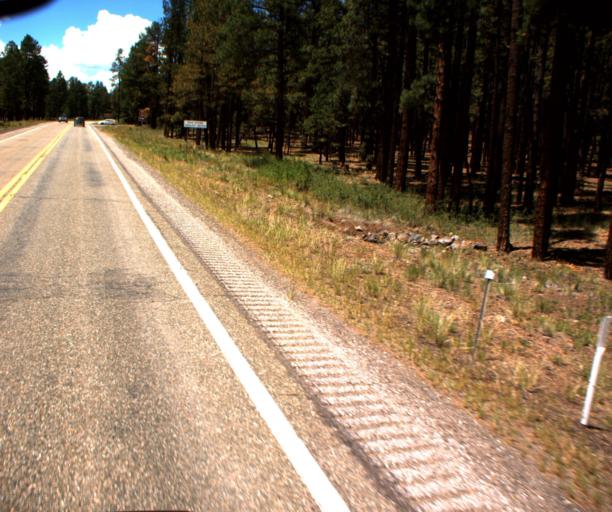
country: US
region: Arizona
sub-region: Coconino County
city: Flagstaff
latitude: 35.2856
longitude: -111.7556
